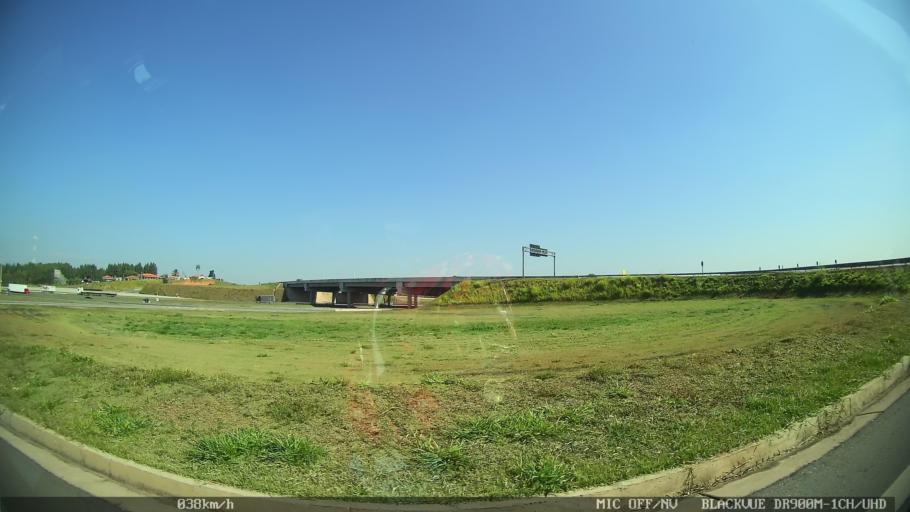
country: BR
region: Sao Paulo
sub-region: Valinhos
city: Valinhos
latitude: -23.0138
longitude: -47.0833
